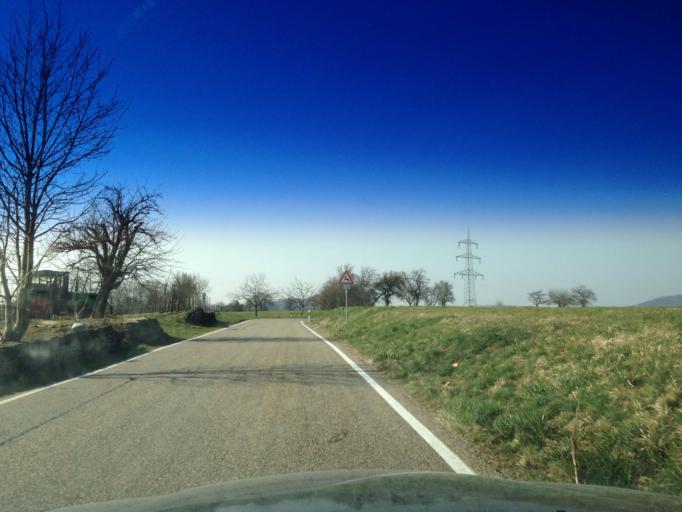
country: DE
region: Baden-Wuerttemberg
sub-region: Karlsruhe Region
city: Illingen
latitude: 48.9473
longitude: 8.9049
